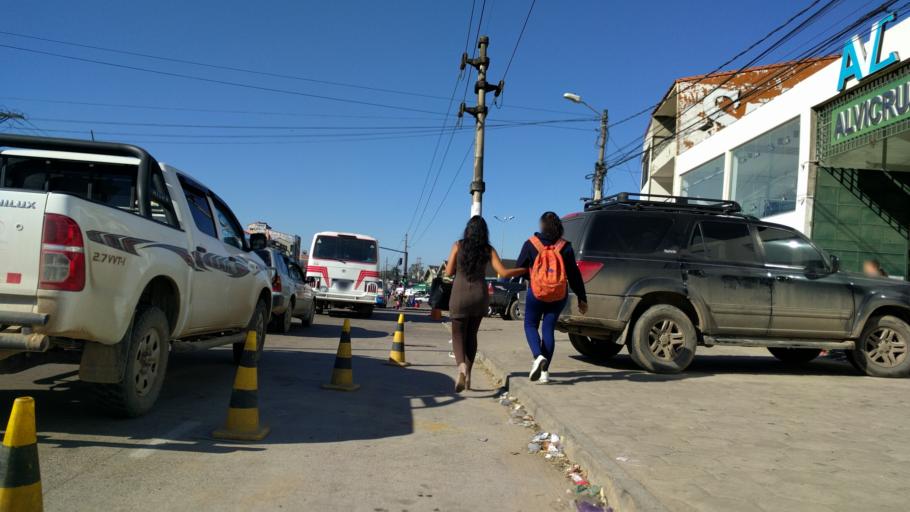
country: BO
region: Santa Cruz
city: Santa Cruz de la Sierra
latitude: -17.7935
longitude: -63.2045
